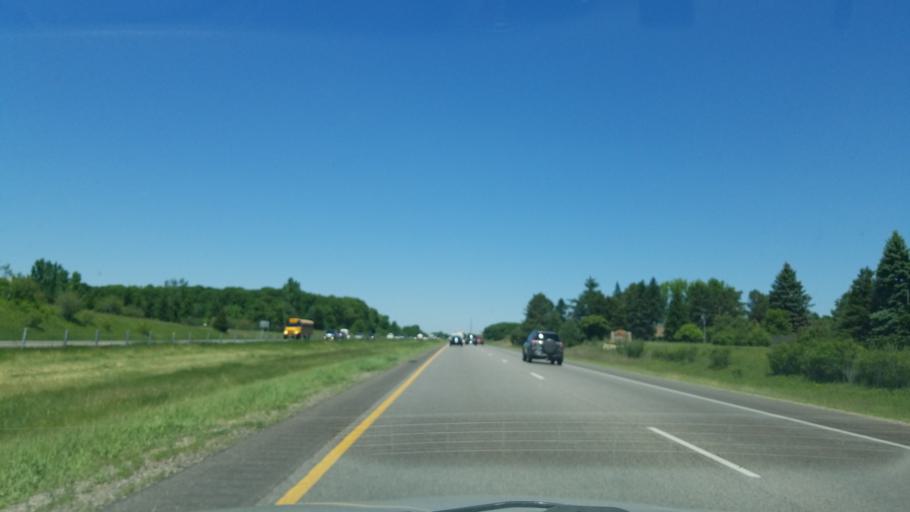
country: US
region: Minnesota
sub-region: Chisago County
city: Wyoming
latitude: 45.3135
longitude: -93.0034
